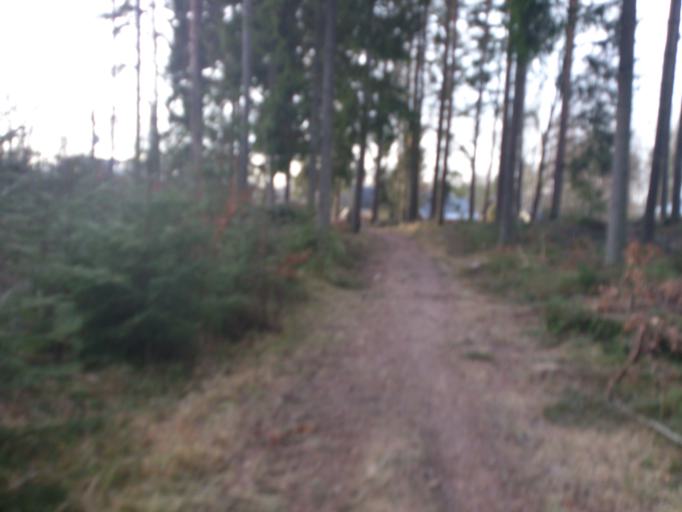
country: SE
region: Kronoberg
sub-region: Alvesta Kommun
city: Moheda
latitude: 56.9977
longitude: 14.5851
